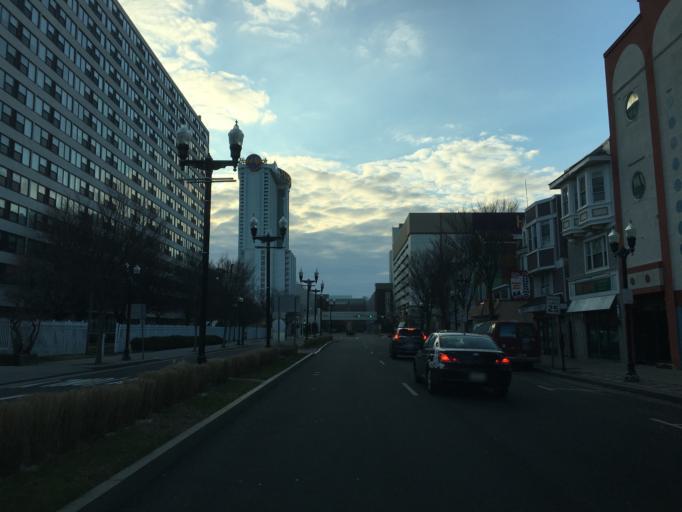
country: US
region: New Jersey
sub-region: Atlantic County
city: Atlantic City
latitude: 39.3638
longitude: -74.4227
